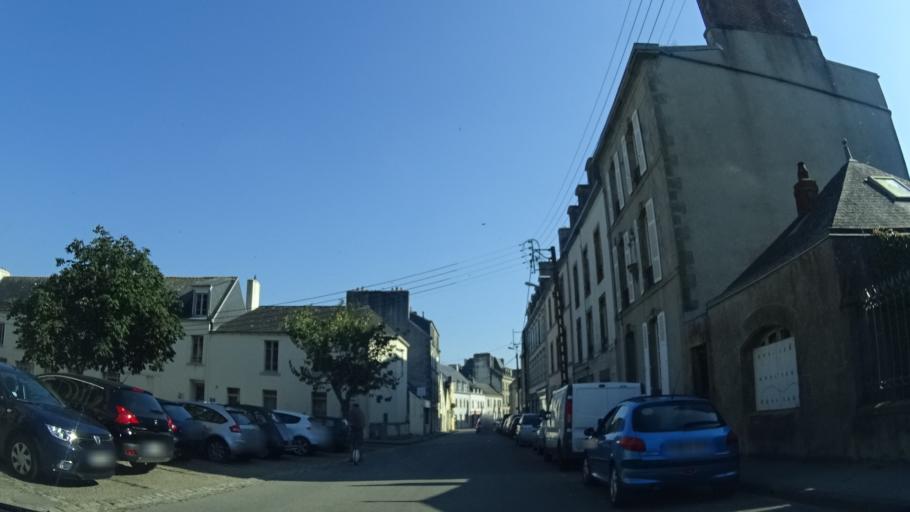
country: FR
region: Brittany
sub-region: Departement du Finistere
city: Douarnenez
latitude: 48.0949
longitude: -4.3307
